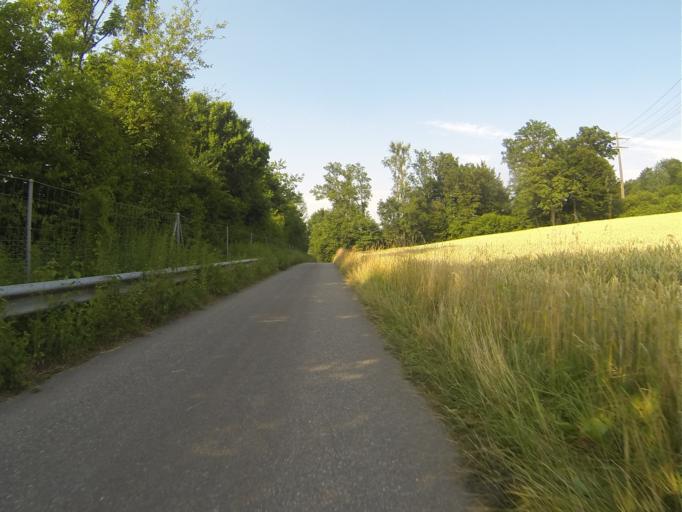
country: CH
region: Lucerne
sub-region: Lucerne-Land District
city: Ebikon
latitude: 47.0827
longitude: 8.3199
